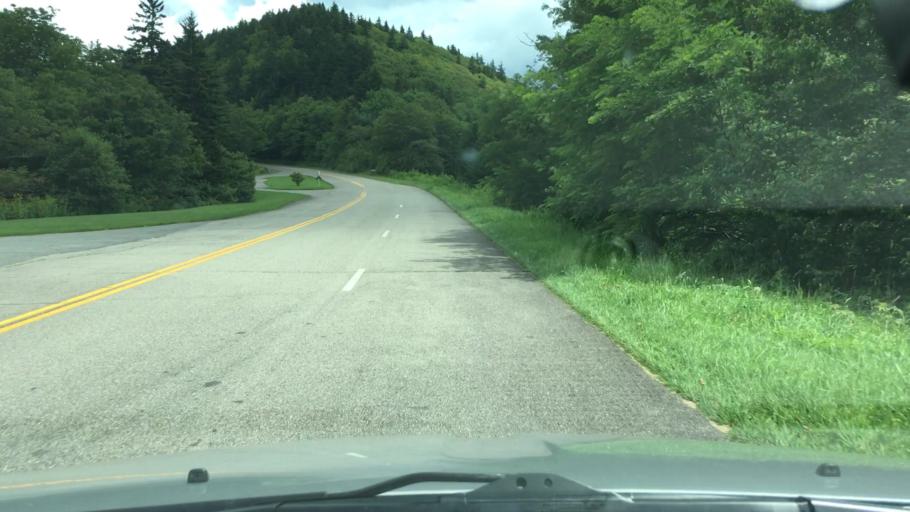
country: US
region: North Carolina
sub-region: Buncombe County
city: Black Mountain
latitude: 35.7179
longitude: -82.2796
